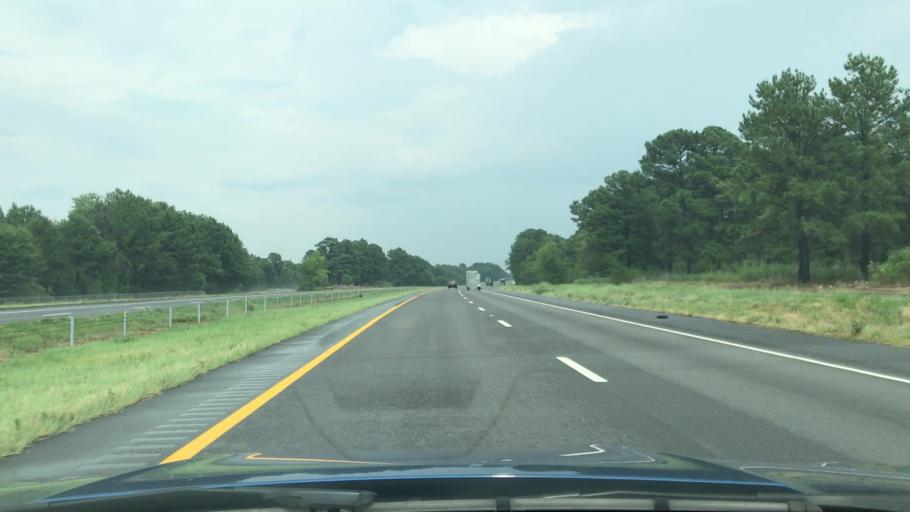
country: US
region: Texas
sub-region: Harrison County
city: Hallsville
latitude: 32.4839
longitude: -94.5256
